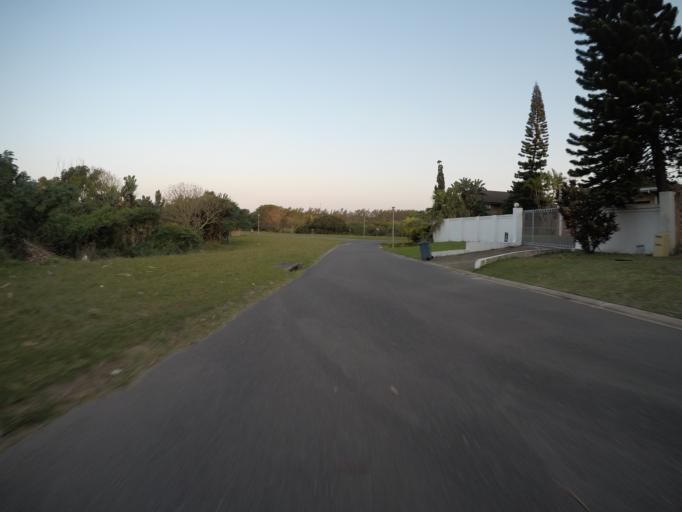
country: ZA
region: KwaZulu-Natal
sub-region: uThungulu District Municipality
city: Richards Bay
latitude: -28.7681
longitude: 32.1231
